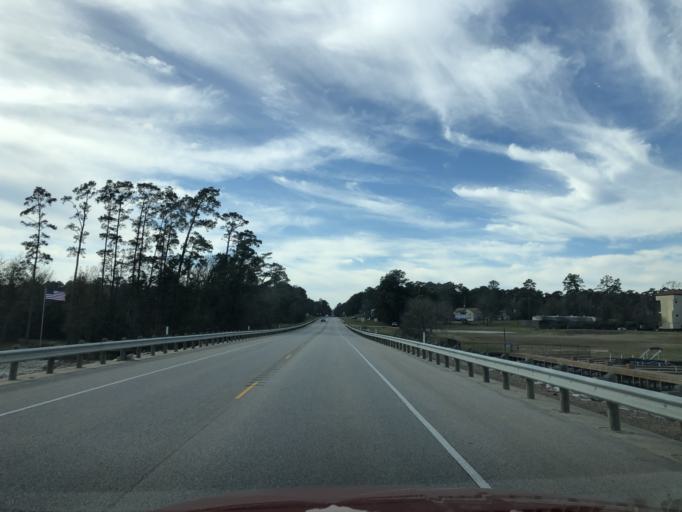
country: US
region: Texas
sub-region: Montgomery County
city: Panorama Village
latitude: 30.4372
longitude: -95.6106
